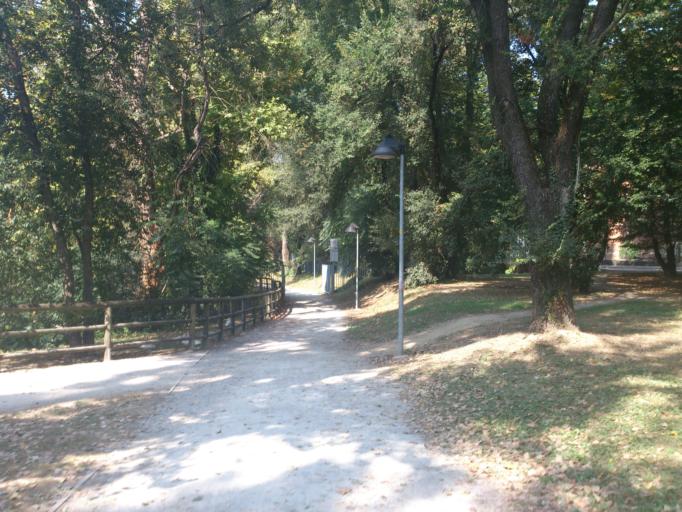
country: IT
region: Lombardy
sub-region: Citta metropolitana di Milano
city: San Donato Milanese
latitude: 45.4165
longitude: 9.2767
